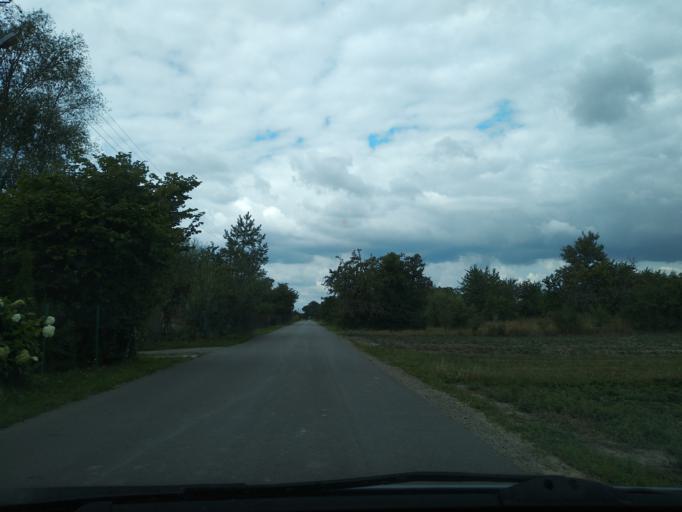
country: PL
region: Lublin Voivodeship
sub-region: Powiat lubartowski
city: Michow
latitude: 51.4960
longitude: 22.2863
